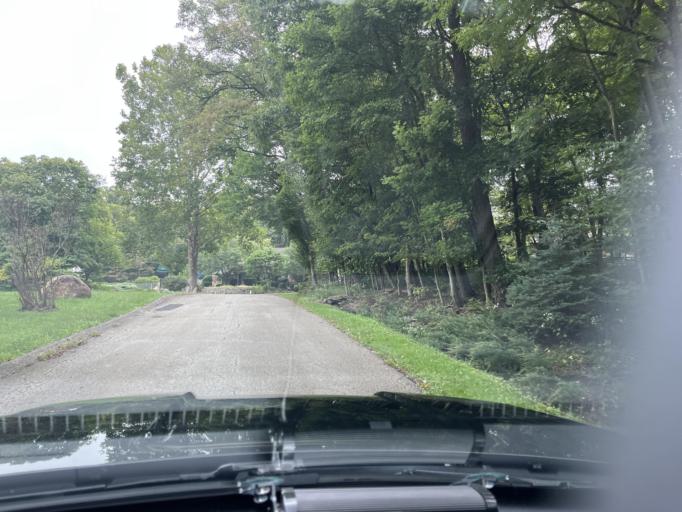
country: US
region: Pennsylvania
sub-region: Fayette County
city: Hopwood
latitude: 39.8637
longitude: -79.6981
